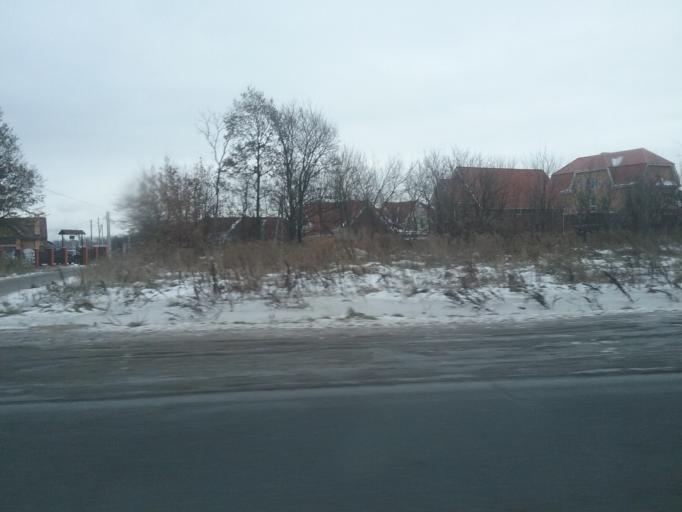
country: RU
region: Tula
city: Tula
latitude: 54.1617
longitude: 37.6372
